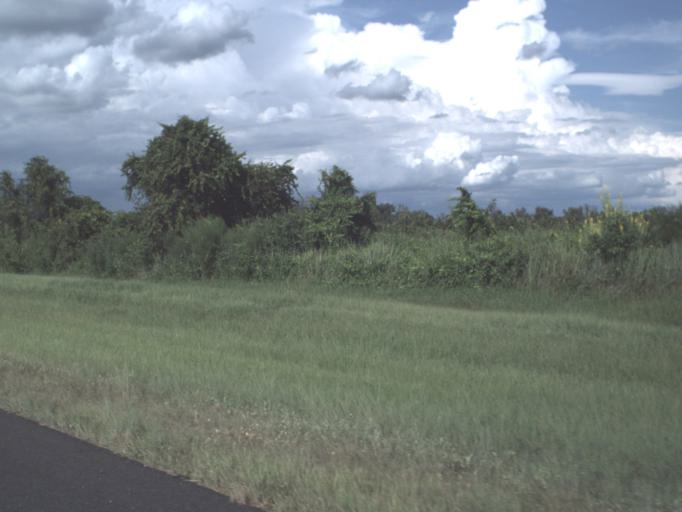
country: US
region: Florida
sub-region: Hardee County
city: Zolfo Springs
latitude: 27.4564
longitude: -81.7969
